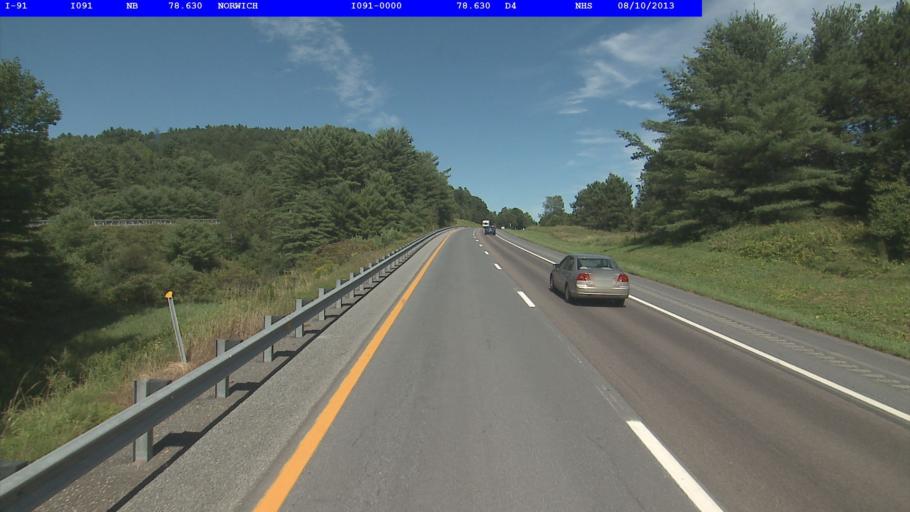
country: US
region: New Hampshire
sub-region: Grafton County
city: Hanover
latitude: 43.7463
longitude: -72.2567
